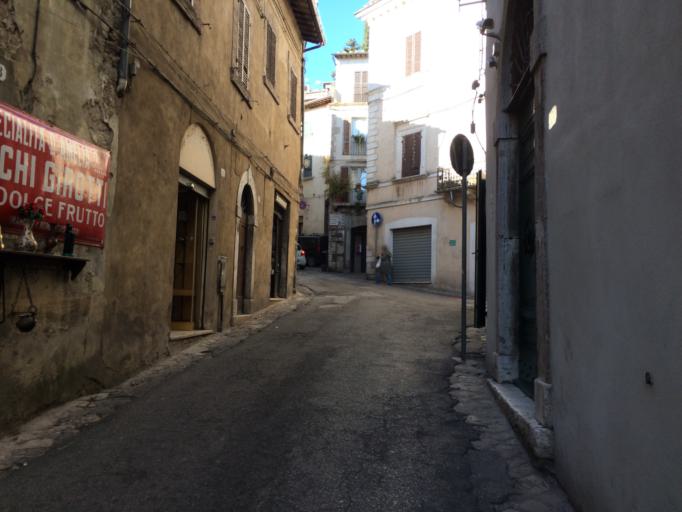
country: IT
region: Umbria
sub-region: Provincia di Terni
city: Amelia
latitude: 42.5556
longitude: 12.4150
